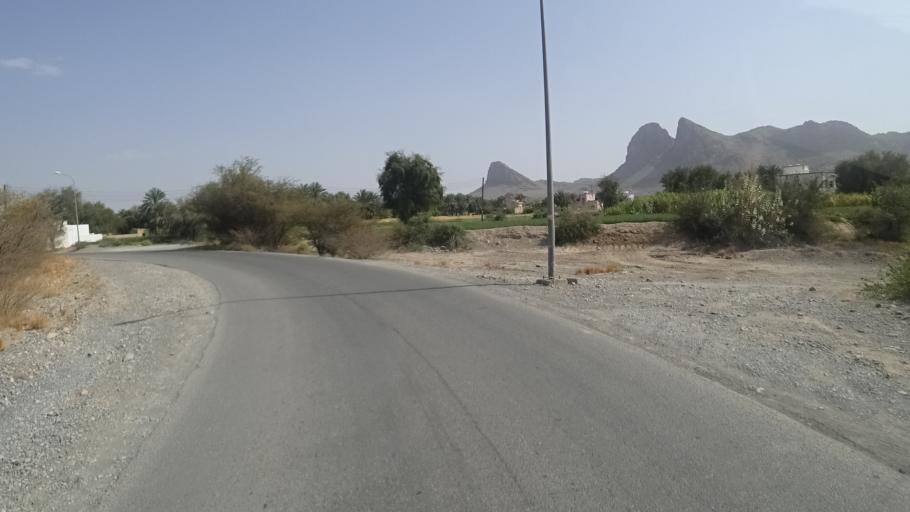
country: OM
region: Muhafazat ad Dakhiliyah
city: Bahla'
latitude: 23.0987
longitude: 57.3023
